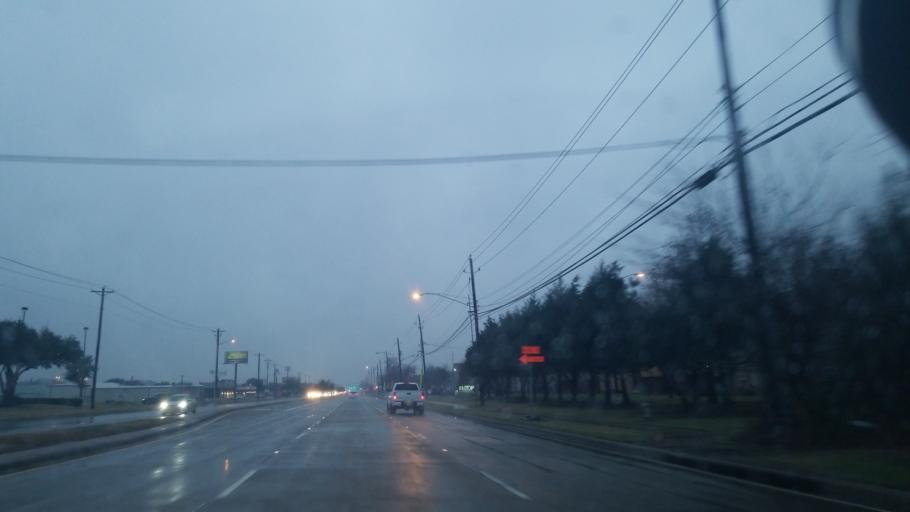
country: US
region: Texas
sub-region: Denton County
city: Denton
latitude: 33.2208
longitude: -97.0905
